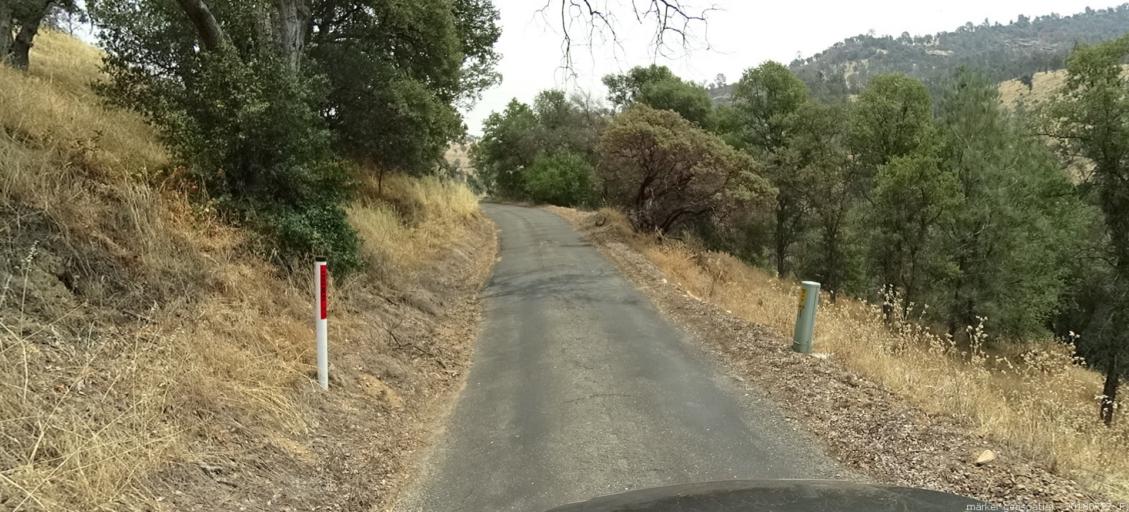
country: US
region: California
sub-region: Madera County
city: Coarsegold
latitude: 37.2650
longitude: -119.6781
